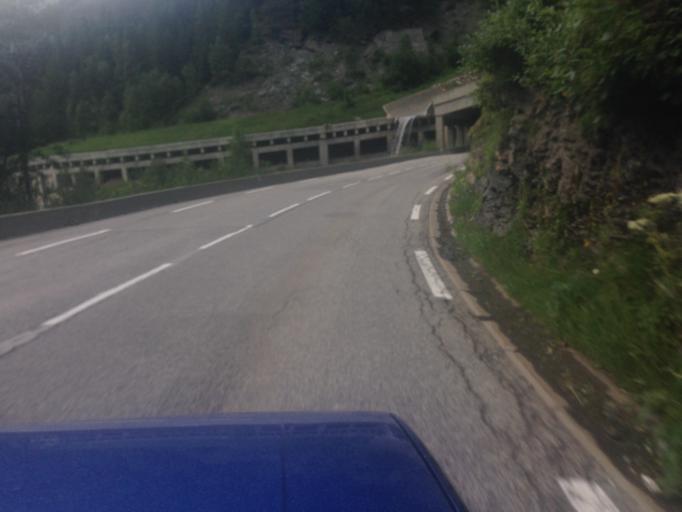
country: FR
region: Rhone-Alpes
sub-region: Departement de la Savoie
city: Tignes
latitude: 45.5308
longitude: 6.9151
